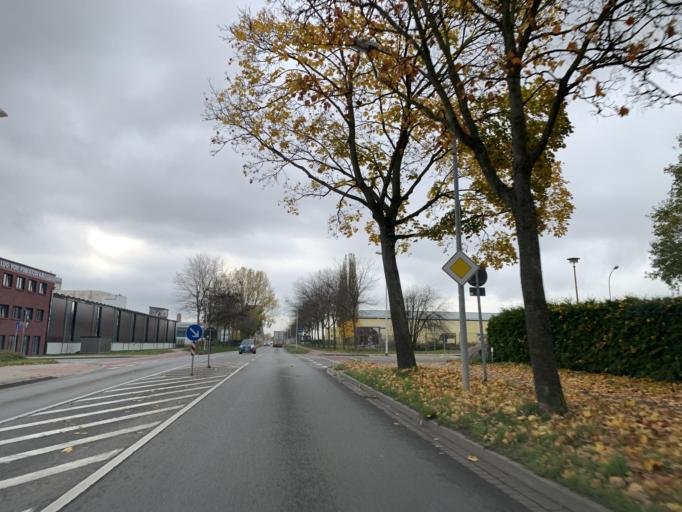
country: DE
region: Mecklenburg-Vorpommern
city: Trollenhagen
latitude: 53.5787
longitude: 13.3057
